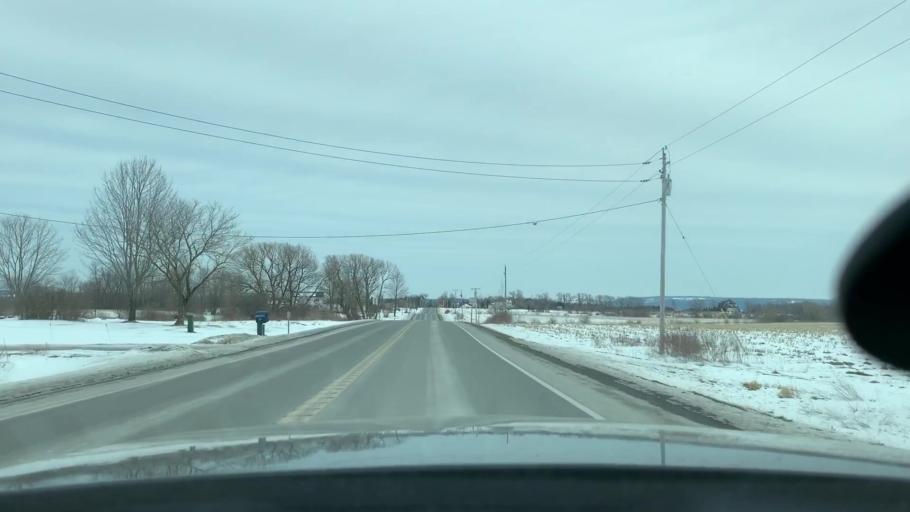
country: US
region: New York
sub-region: Herkimer County
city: Frankfort
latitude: 43.0332
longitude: -75.1192
